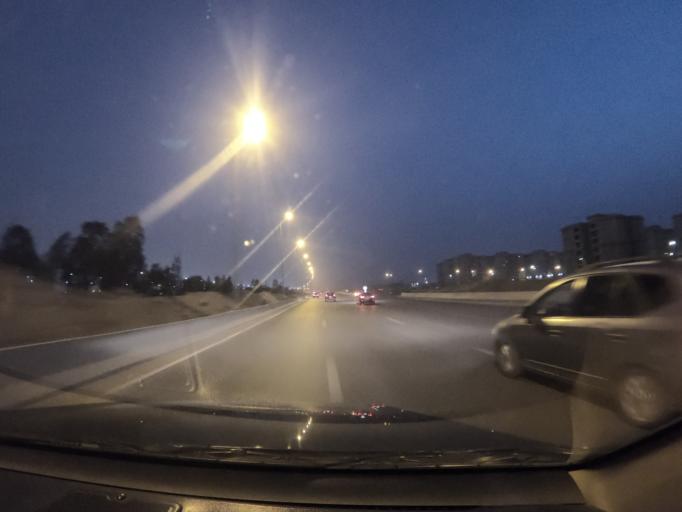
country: EG
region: Muhafazat al Qahirah
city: Cairo
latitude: 30.0389
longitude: 31.4030
